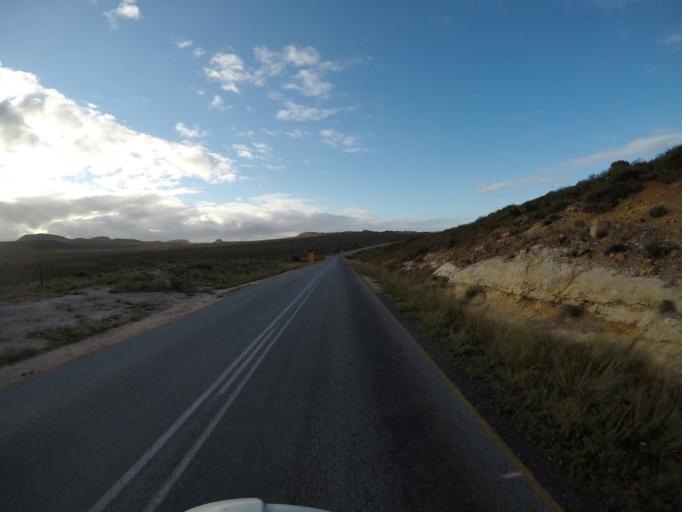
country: ZA
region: Western Cape
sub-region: West Coast District Municipality
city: Clanwilliam
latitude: -32.3305
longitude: 18.3712
